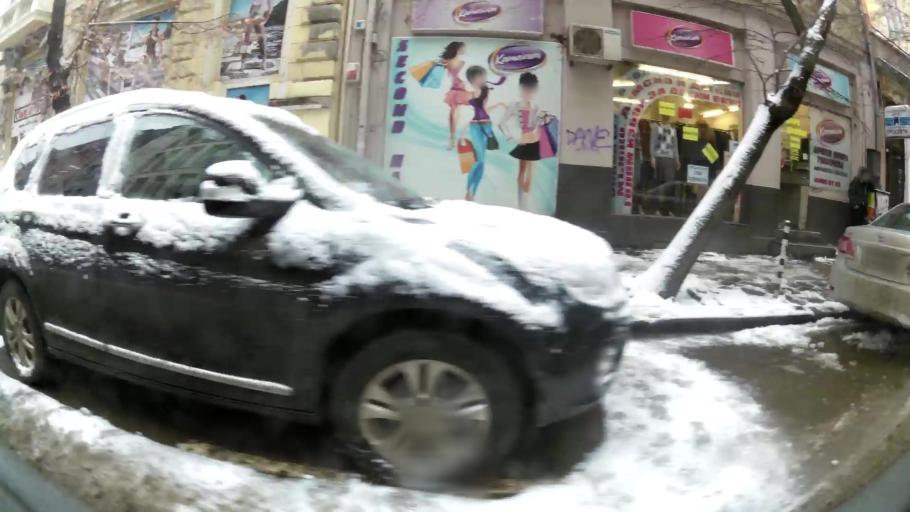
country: BG
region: Sofia-Capital
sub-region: Stolichna Obshtina
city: Sofia
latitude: 42.6969
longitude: 23.3191
